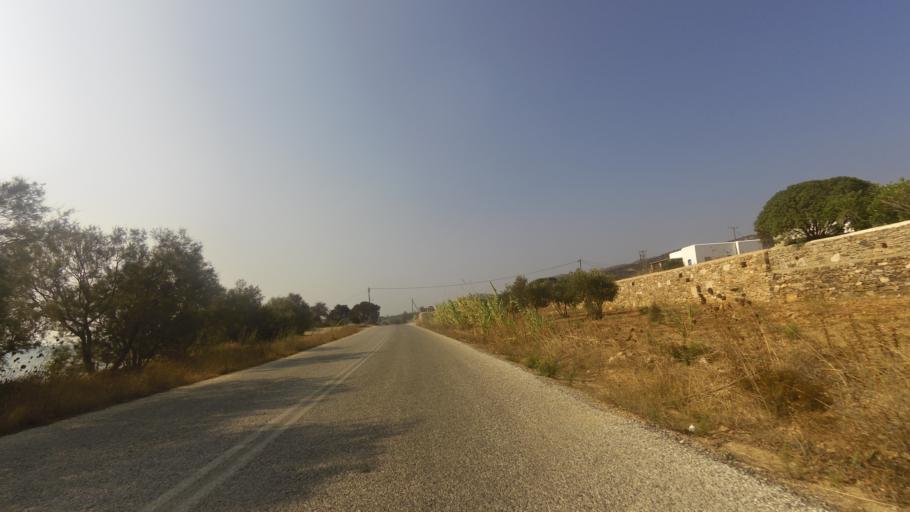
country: GR
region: South Aegean
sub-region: Nomos Kykladon
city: Antiparos
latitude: 37.0106
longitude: 25.0748
